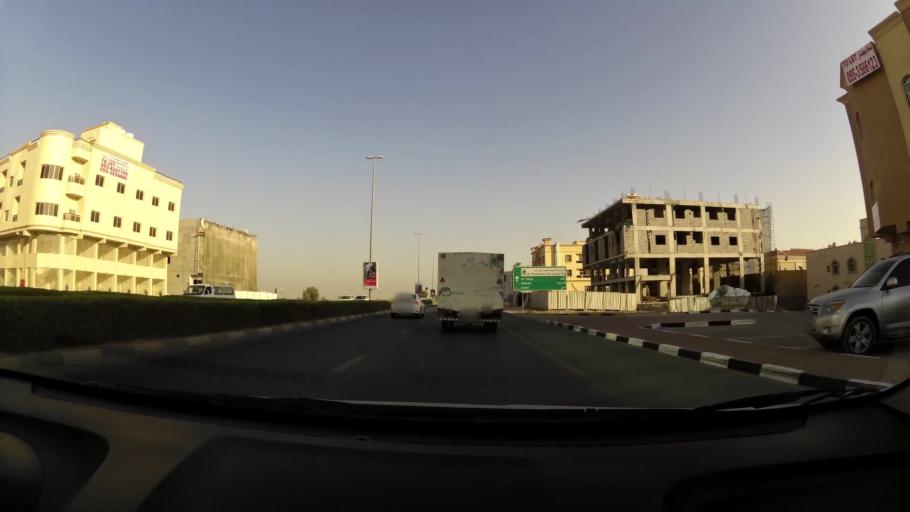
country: AE
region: Ajman
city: Ajman
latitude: 25.3775
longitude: 55.5079
